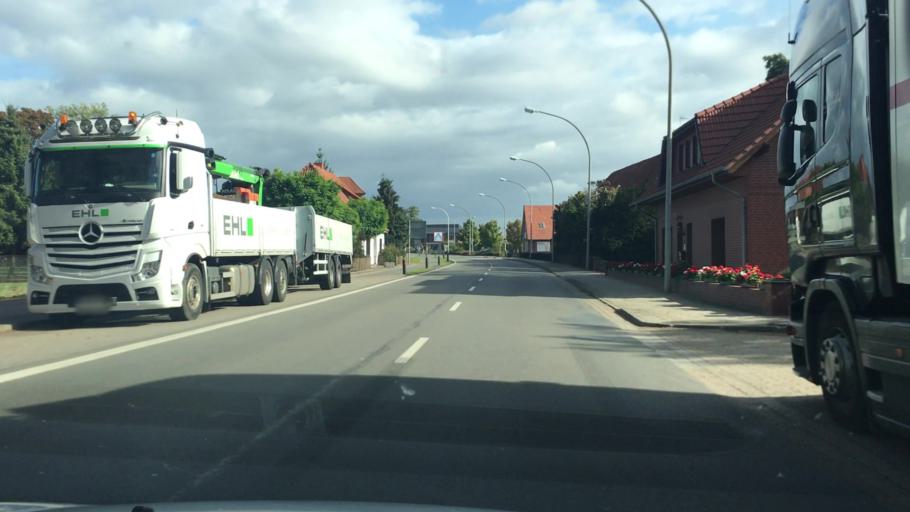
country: DE
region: Lower Saxony
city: Rehden
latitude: 52.6098
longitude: 8.4826
